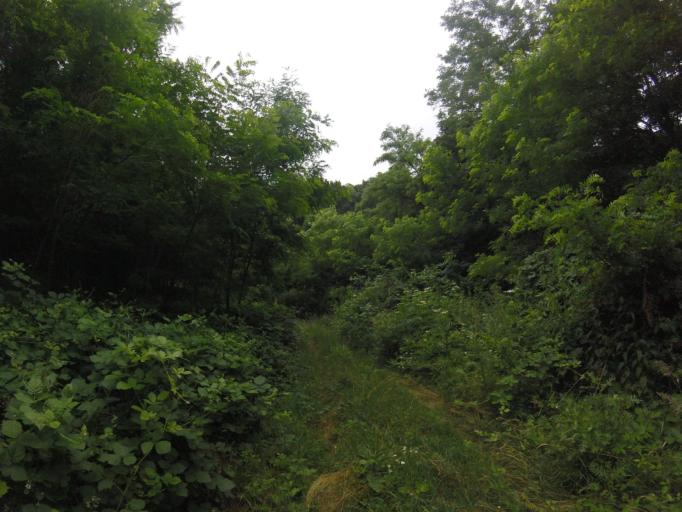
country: HU
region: Nograd
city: Romhany
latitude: 47.9052
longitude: 19.2918
